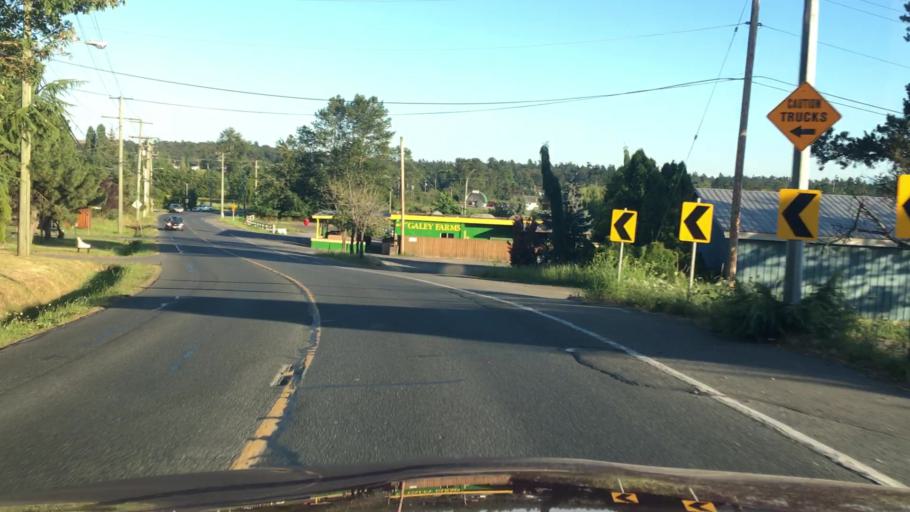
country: CA
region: British Columbia
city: Victoria
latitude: 48.4784
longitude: -123.3542
